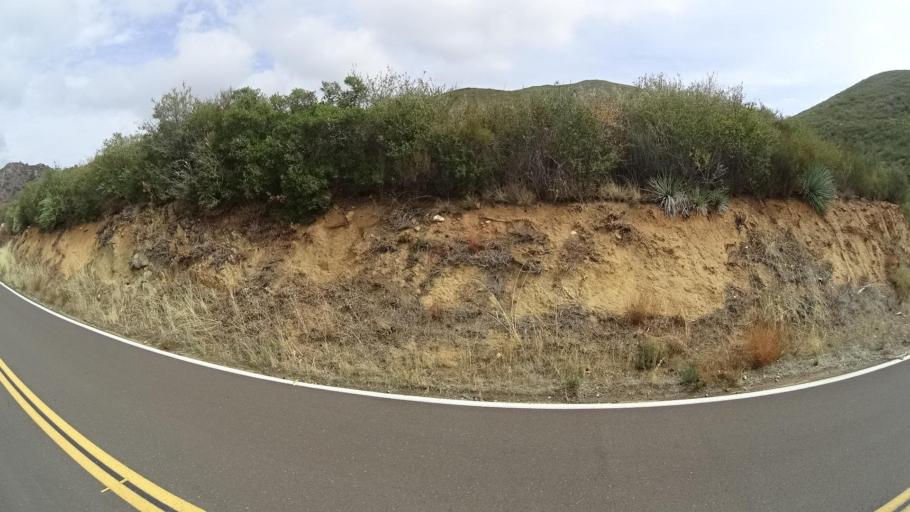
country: US
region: California
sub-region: San Diego County
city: Descanso
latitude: 32.8924
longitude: -116.6499
